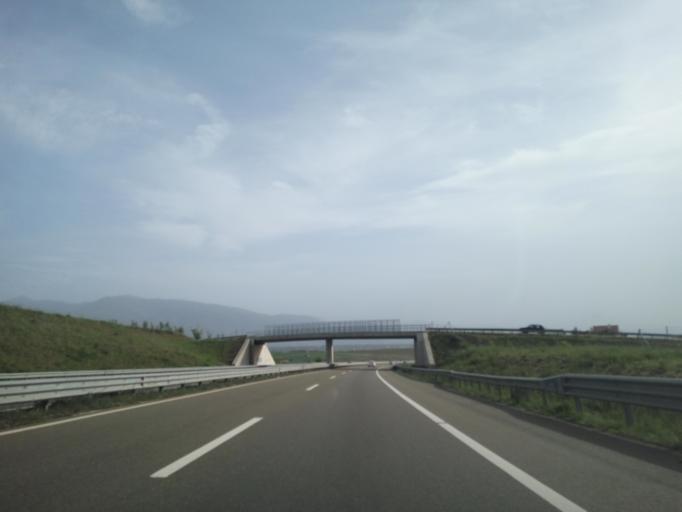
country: XK
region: Prizren
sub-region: Komuna e Therandes
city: Peqan
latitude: 42.3820
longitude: 20.8467
